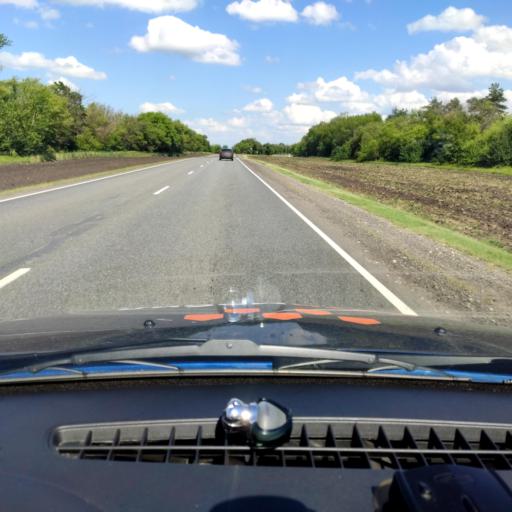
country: RU
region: Orjol
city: Livny
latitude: 52.4304
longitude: 37.7953
